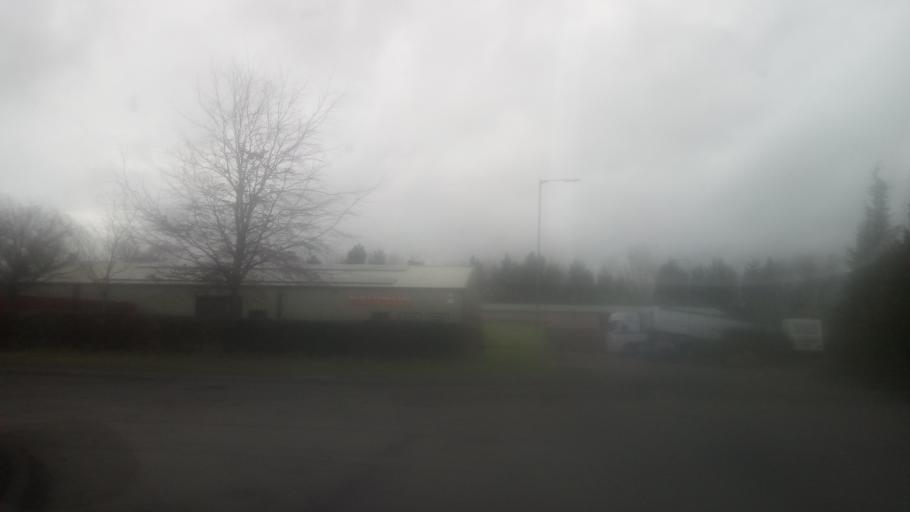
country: GB
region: Scotland
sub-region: The Scottish Borders
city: Jedburgh
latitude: 55.4774
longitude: -2.5363
